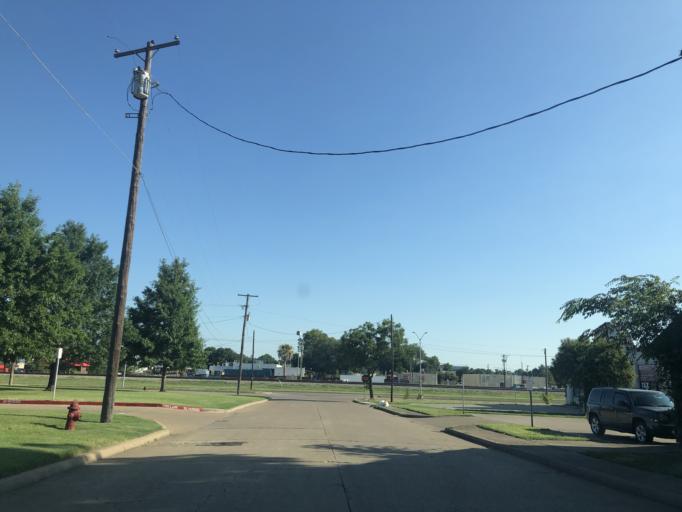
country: US
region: Texas
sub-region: Dallas County
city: Grand Prairie
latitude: 32.7434
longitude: -97.0072
